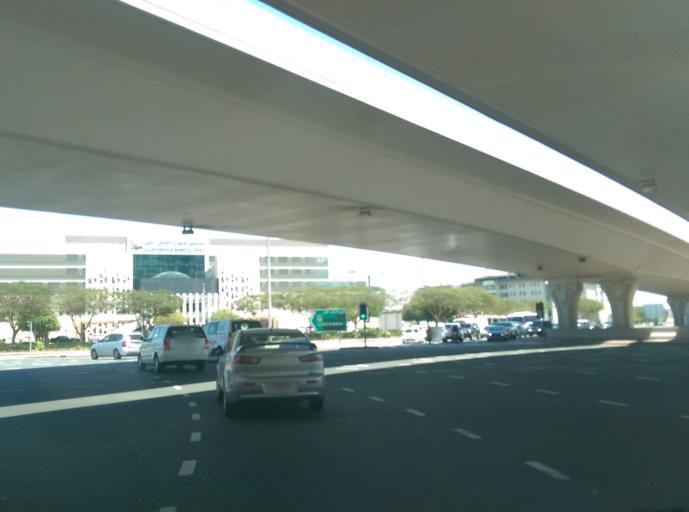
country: AE
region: Dubai
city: Dubai
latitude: 25.0974
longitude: 55.1815
